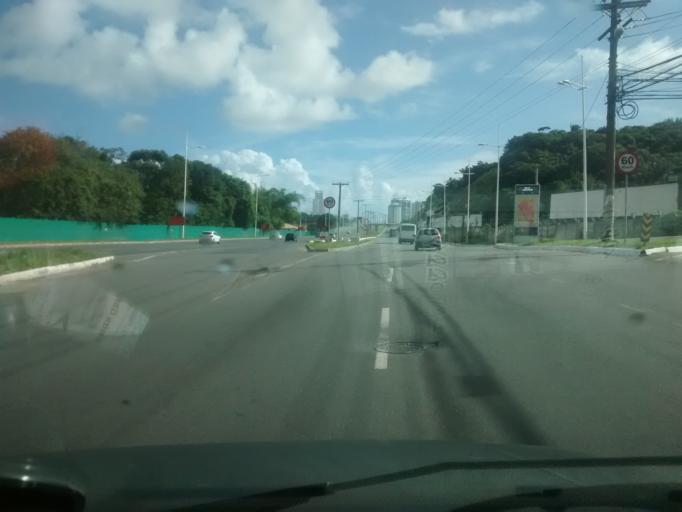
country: BR
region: Bahia
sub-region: Salvador
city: Salvador
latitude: -12.9692
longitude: -38.4426
